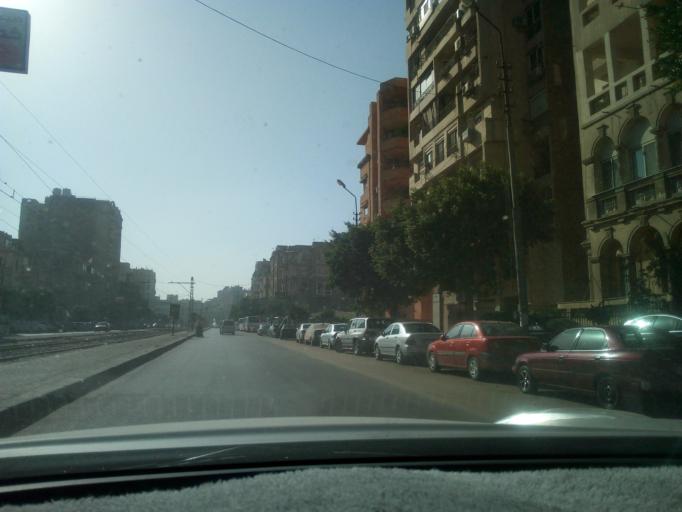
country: EG
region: Muhafazat al Qahirah
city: Cairo
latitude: 30.0997
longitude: 31.3331
